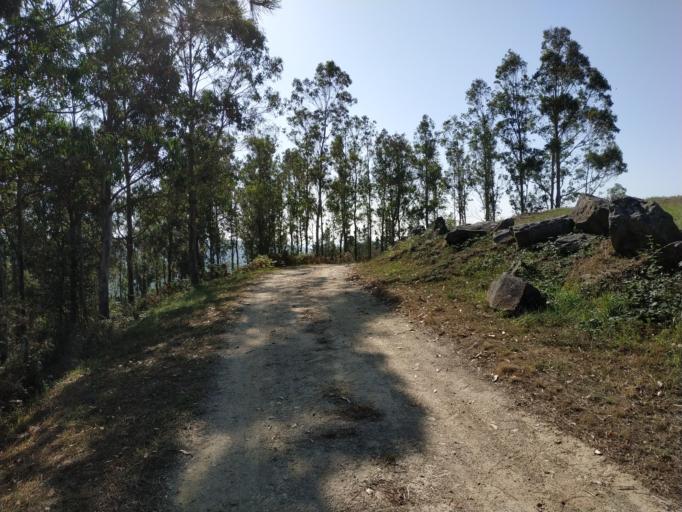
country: ES
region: Galicia
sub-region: Provincia da Coruna
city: Laracha
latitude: 43.2294
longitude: -8.5358
